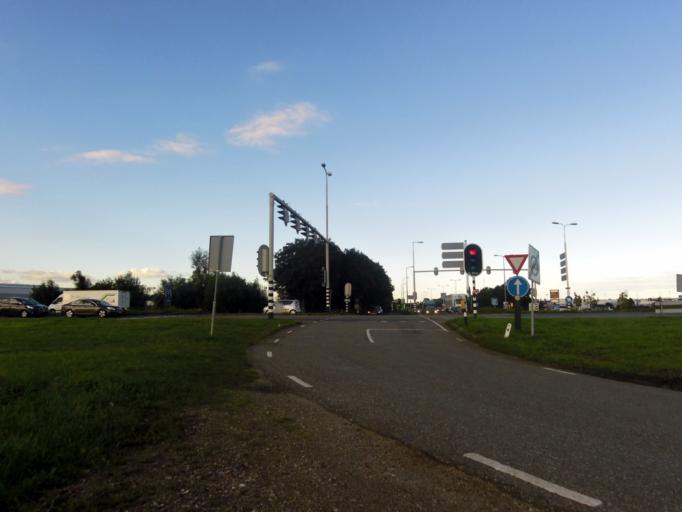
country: NL
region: South Holland
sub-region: Gemeente Alphen aan den Rijn
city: Alphen aan den Rijn
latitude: 52.1232
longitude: 4.6251
